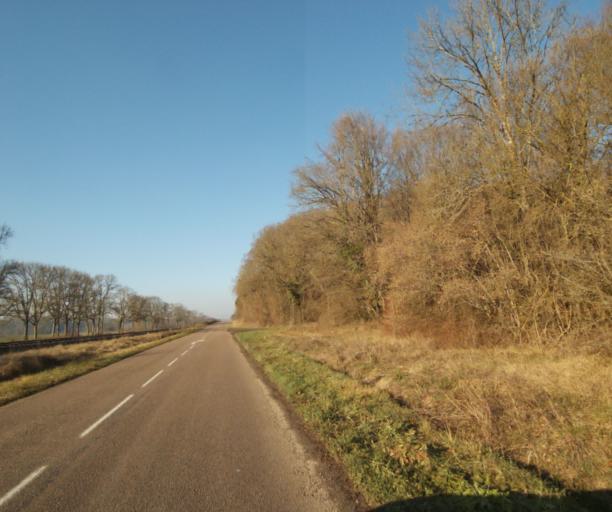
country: FR
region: Champagne-Ardenne
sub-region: Departement de la Haute-Marne
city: Chevillon
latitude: 48.5076
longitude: 5.1240
